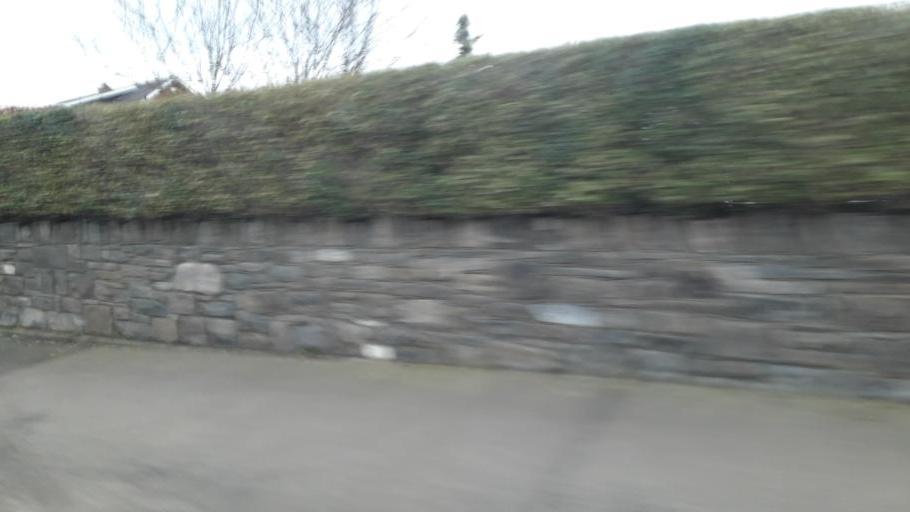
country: IE
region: Leinster
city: An Ros
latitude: 53.5209
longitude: -6.1092
